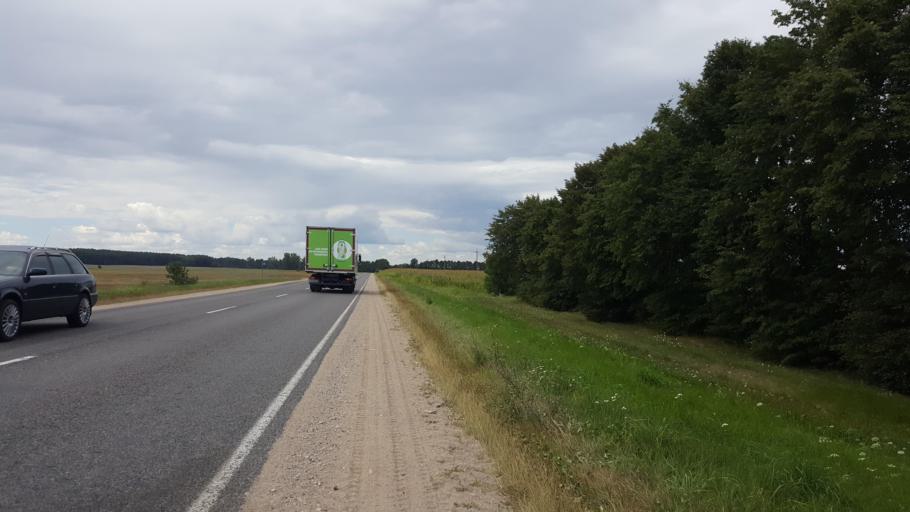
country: BY
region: Brest
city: Kamyanyets
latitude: 52.3647
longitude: 23.8886
